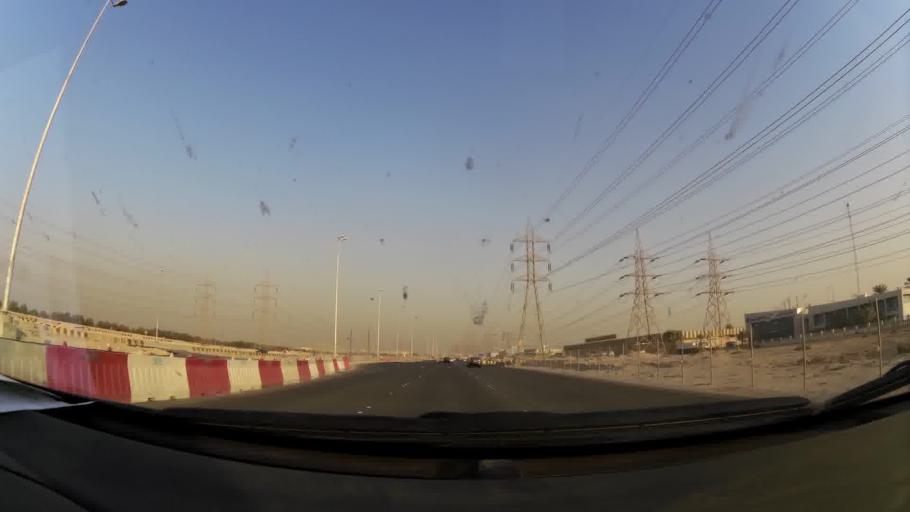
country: KW
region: Al Asimah
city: Ar Rabiyah
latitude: 29.2948
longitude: 47.8407
